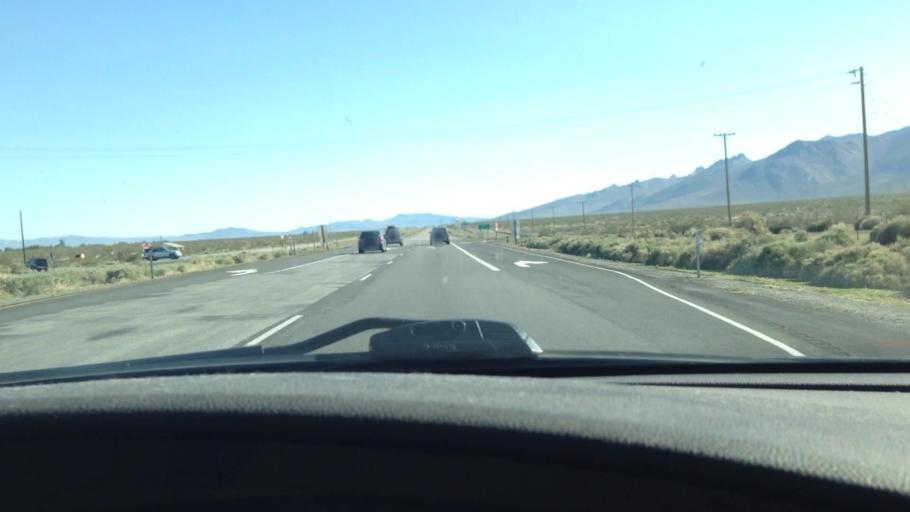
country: US
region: California
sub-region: Kern County
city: Inyokern
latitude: 35.7996
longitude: -117.8730
